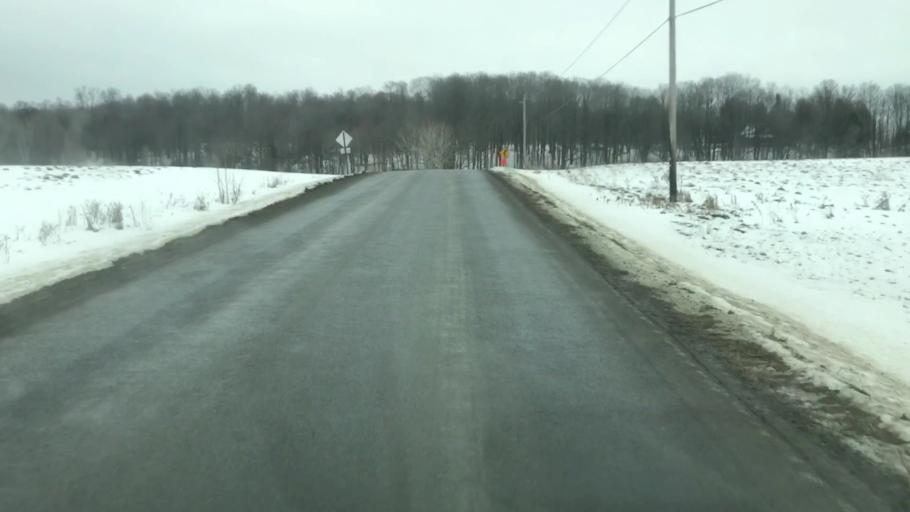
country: US
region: New York
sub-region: Cortland County
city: Cortland West
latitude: 42.6529
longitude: -76.2746
